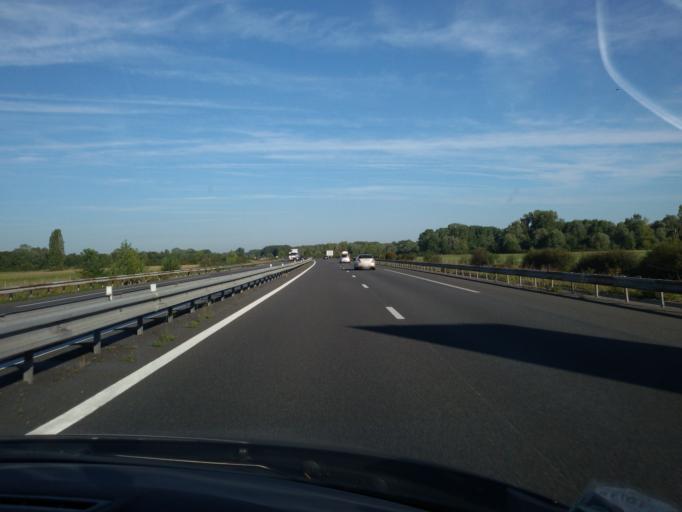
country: FR
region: Centre
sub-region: Departement du Cher
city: Vignoux-sur-Barangeon
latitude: 47.1928
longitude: 2.1582
